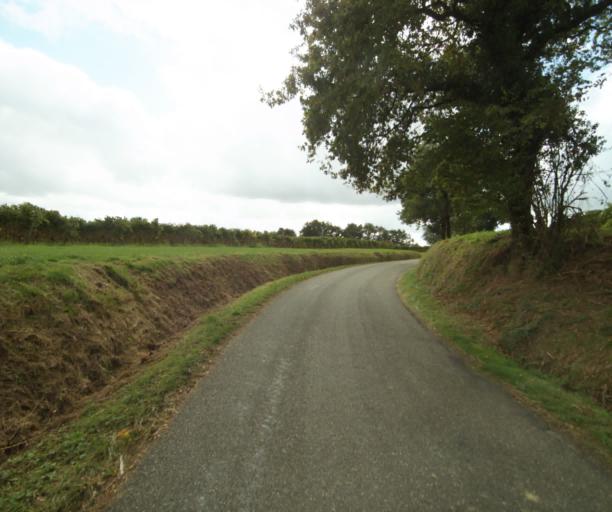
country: FR
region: Midi-Pyrenees
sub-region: Departement du Gers
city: Nogaro
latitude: 43.8484
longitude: -0.0187
